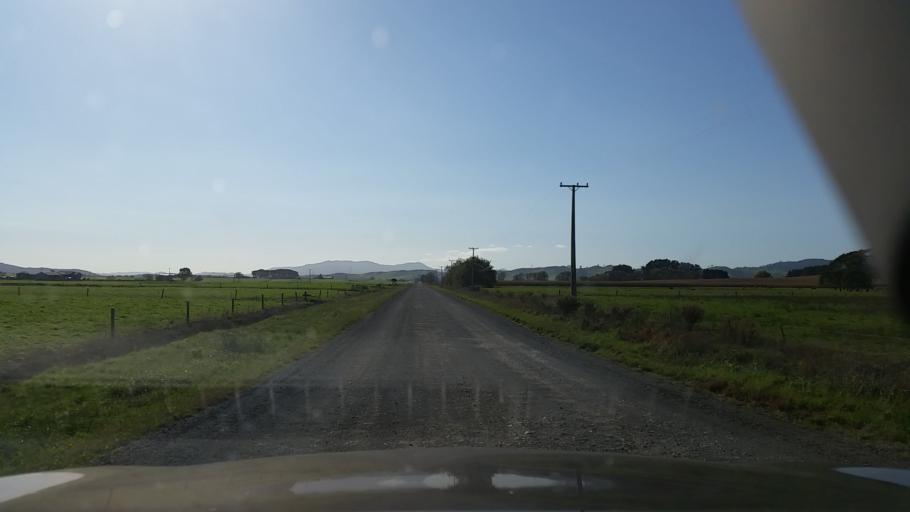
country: NZ
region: Waikato
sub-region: Hamilton City
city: Hamilton
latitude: -37.6372
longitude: 175.4302
